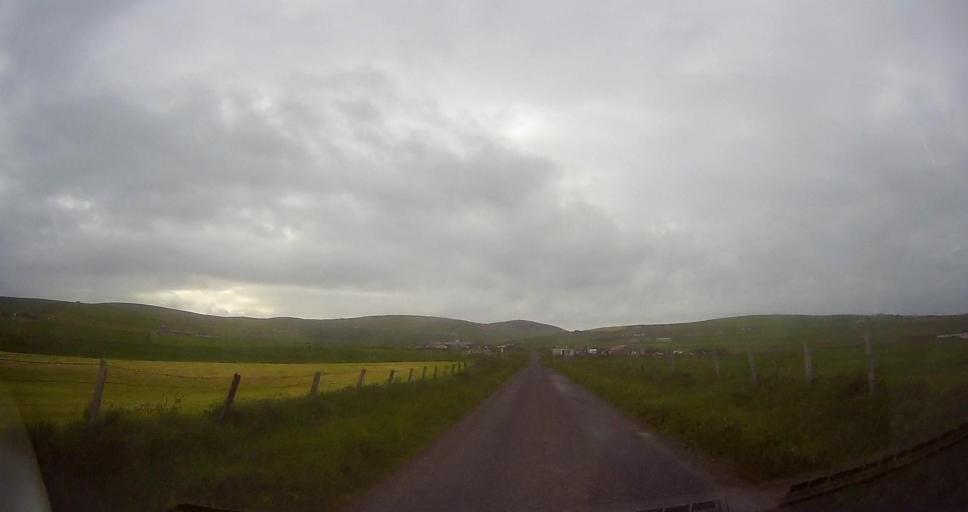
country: GB
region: Scotland
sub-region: Orkney Islands
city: Stromness
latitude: 58.9880
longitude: -3.2787
